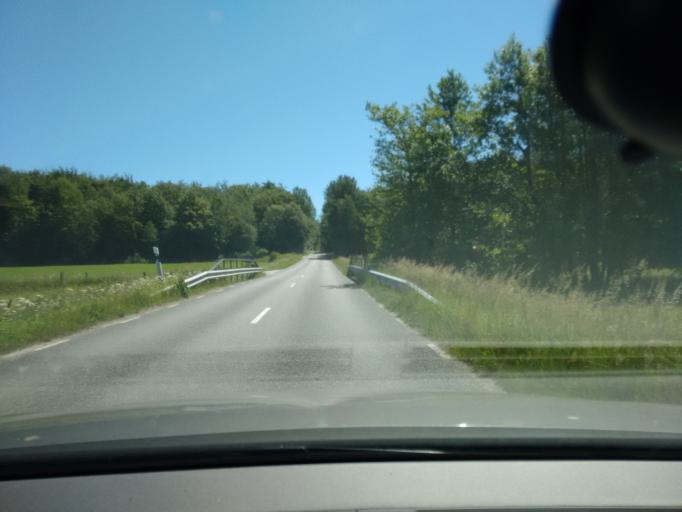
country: SE
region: Skane
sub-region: Kristianstads Kommun
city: Degeberga
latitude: 55.7769
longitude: 13.8914
